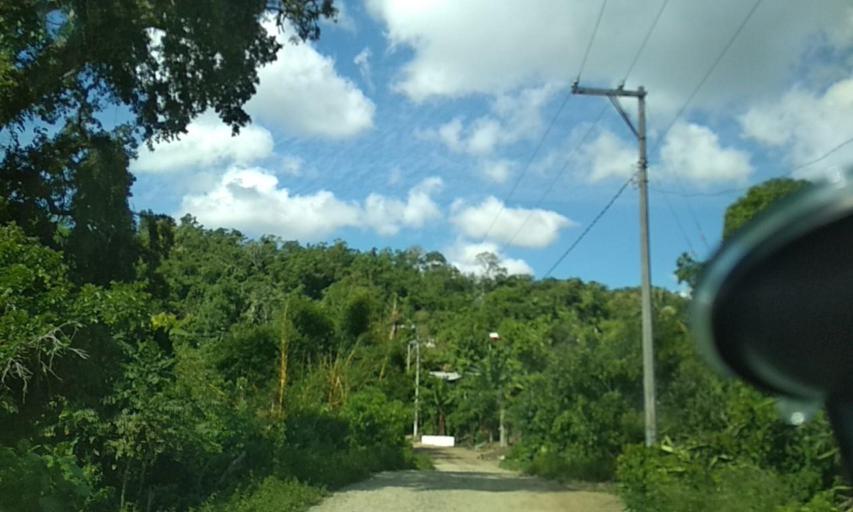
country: MX
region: Veracruz
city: Cazones de Herrera
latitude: 20.6232
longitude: -97.3251
